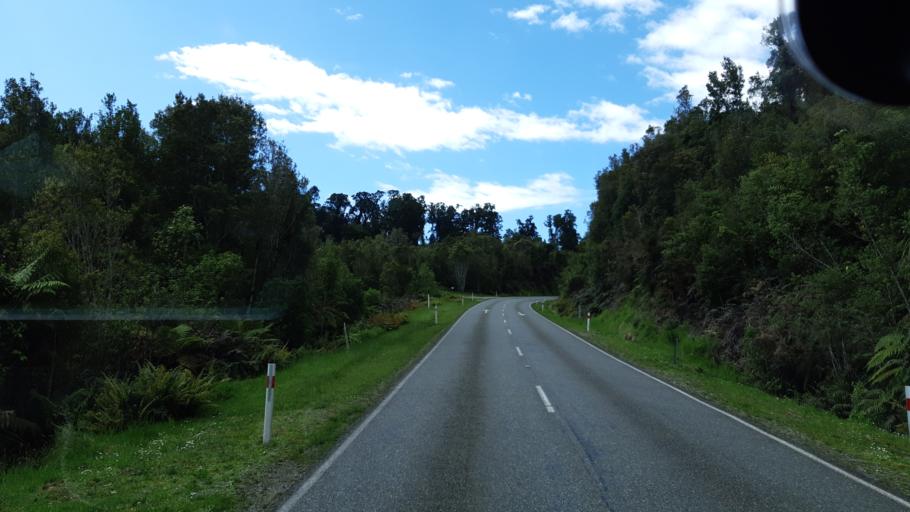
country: NZ
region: West Coast
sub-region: Westland District
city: Hokitika
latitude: -43.0445
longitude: 170.6393
